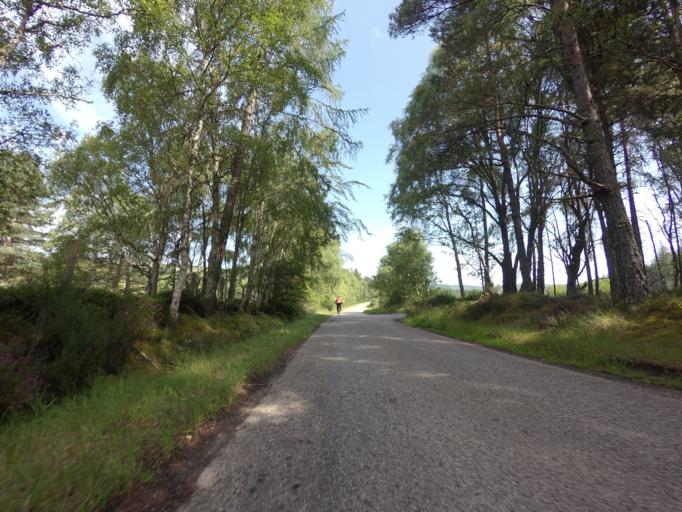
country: GB
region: Scotland
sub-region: Highland
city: Invergordon
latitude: 57.7332
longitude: -4.1912
